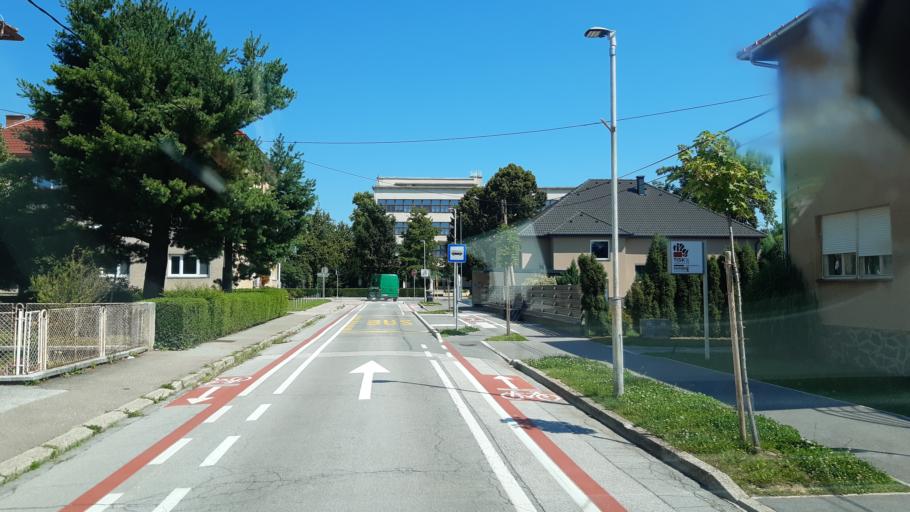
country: SI
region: Murska Sobota
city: Murska Sobota
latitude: 46.6602
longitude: 16.1556
